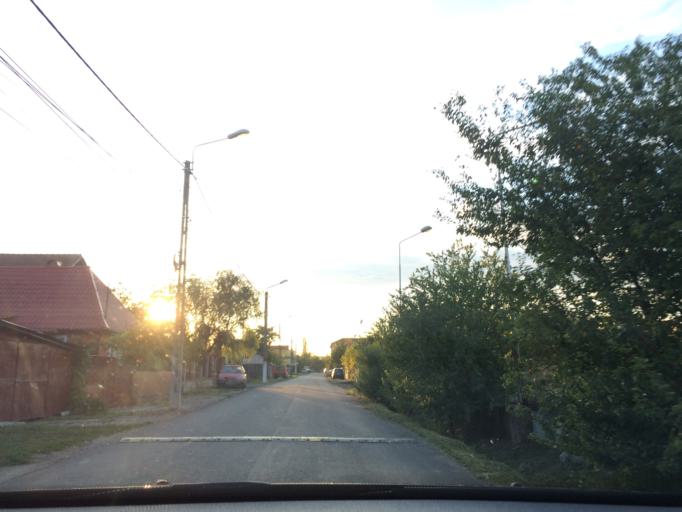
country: RO
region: Timis
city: Timisoara
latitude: 45.7632
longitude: 21.1865
